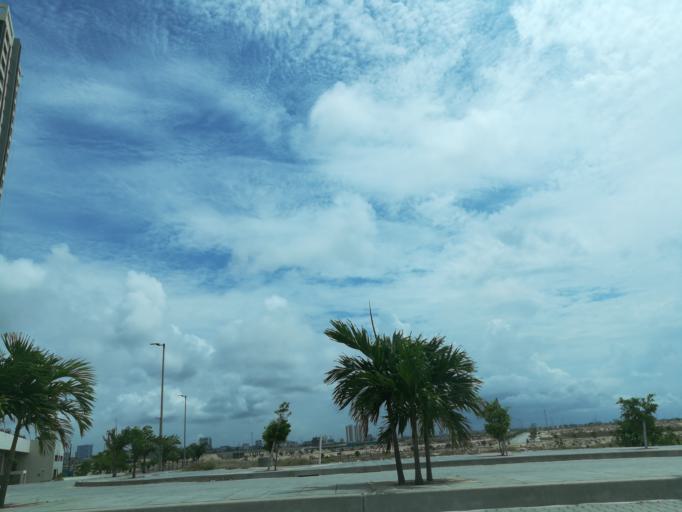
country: NG
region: Lagos
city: Lagos
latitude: 6.4081
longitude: 3.4104
